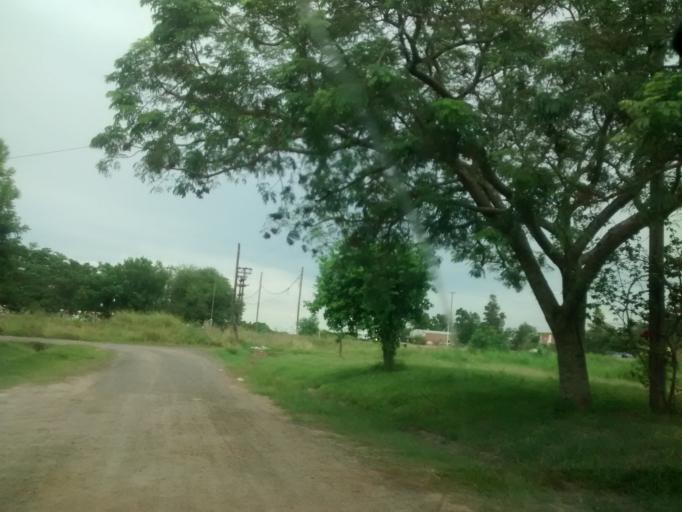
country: AR
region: Chaco
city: Fontana
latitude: -27.4575
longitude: -59.0353
